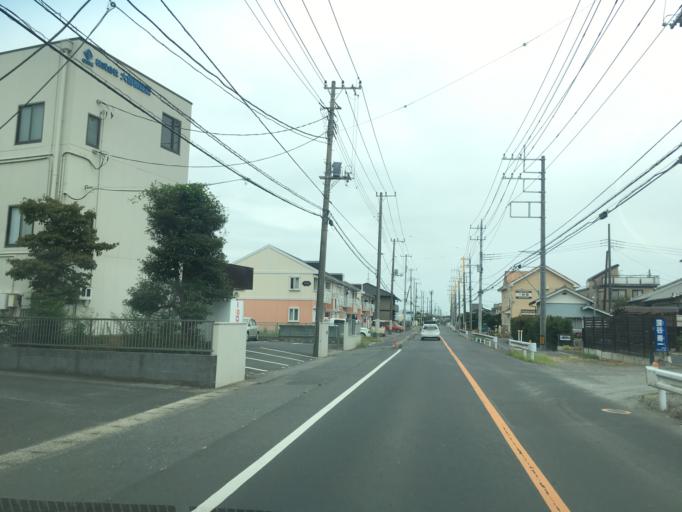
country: JP
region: Ibaraki
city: Hitachi-Naka
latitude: 36.4028
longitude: 140.5546
